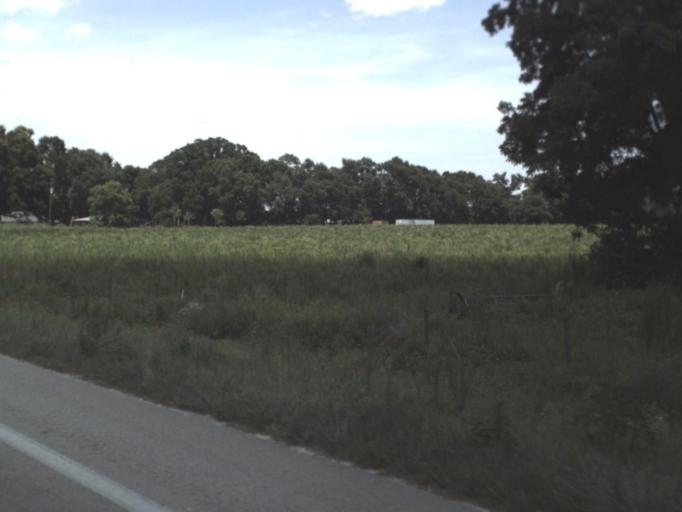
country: US
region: Florida
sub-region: Gilchrist County
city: Trenton
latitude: 29.7137
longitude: -82.8576
